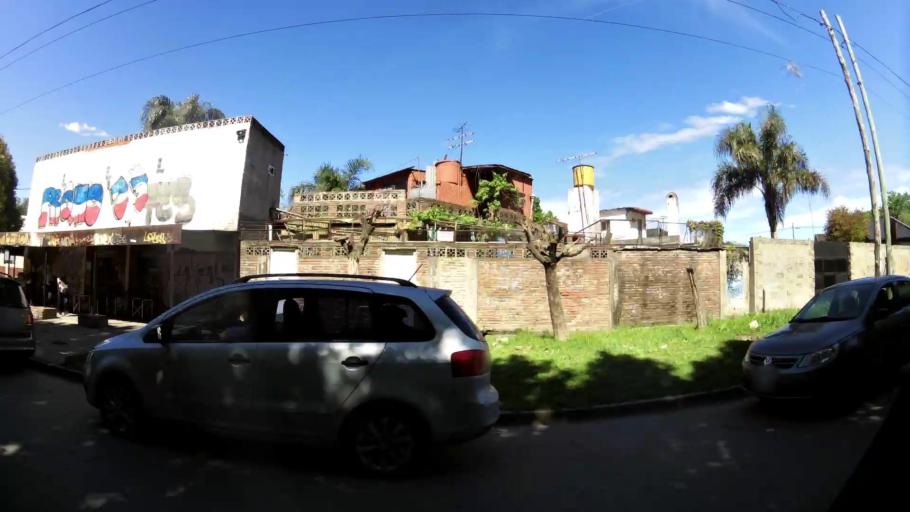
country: AR
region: Buenos Aires
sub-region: Partido de Almirante Brown
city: Adrogue
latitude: -34.7934
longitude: -58.3634
